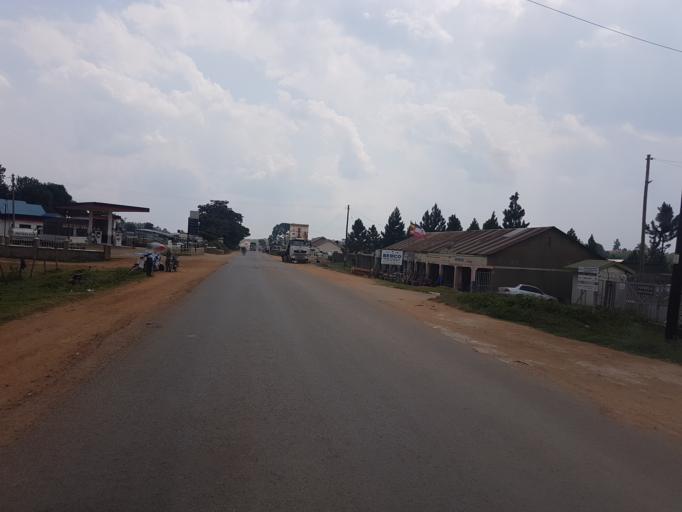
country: UG
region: Western Region
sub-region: Bushenyi District
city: Bushenyi
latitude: -0.5404
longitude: 30.1297
